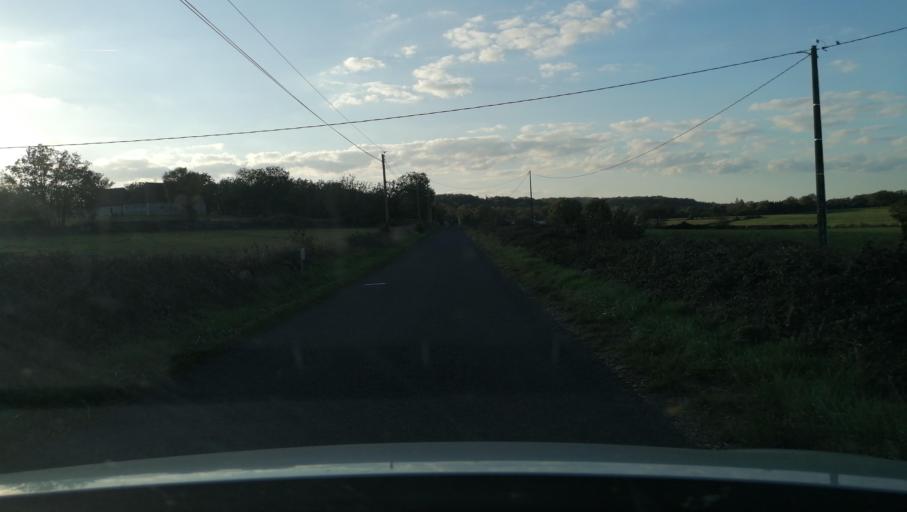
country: FR
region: Midi-Pyrenees
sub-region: Departement du Lot
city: Vayrac
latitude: 44.8714
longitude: 1.6313
